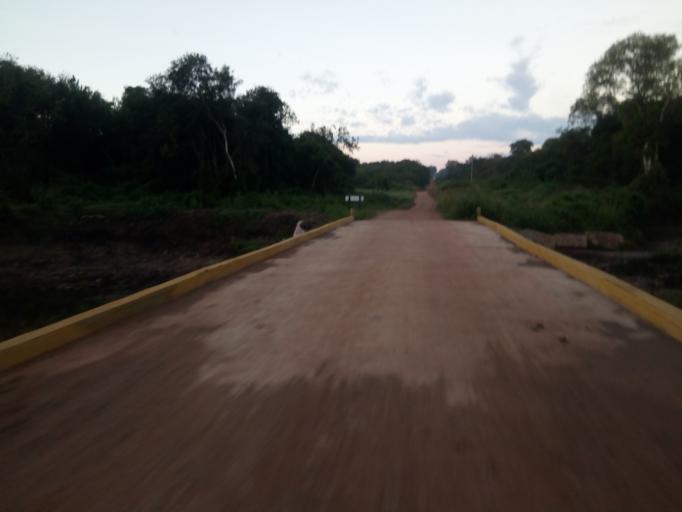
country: AR
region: Misiones
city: Almafuerte
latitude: -27.5659
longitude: -55.4137
